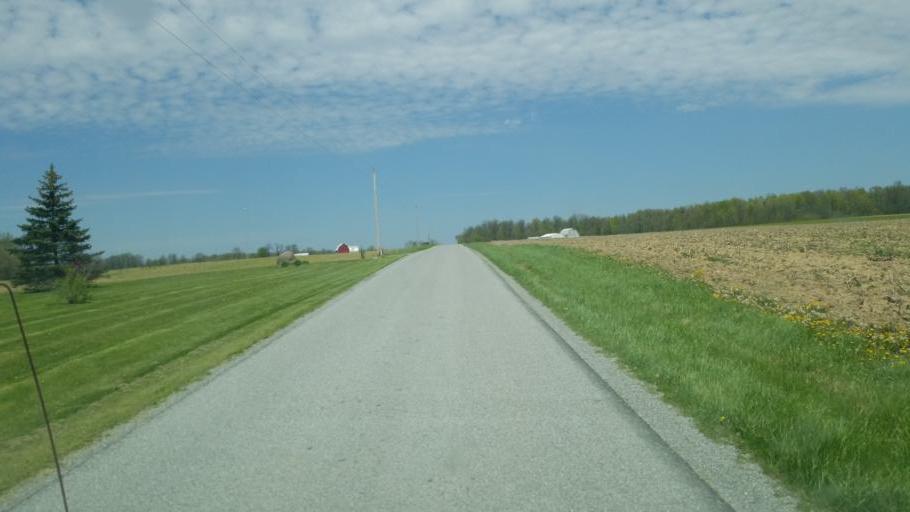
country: US
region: Ohio
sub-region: Hardin County
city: Ada
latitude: 40.7906
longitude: -83.8989
